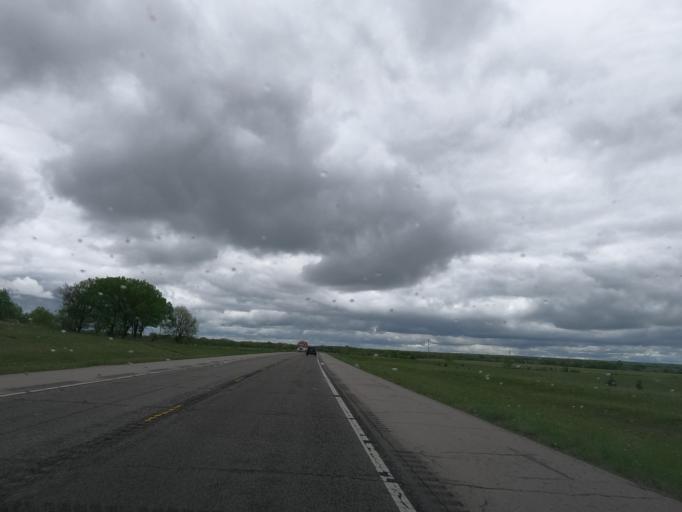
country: US
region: Kansas
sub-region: Montgomery County
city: Cherryvale
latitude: 37.3459
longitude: -95.4680
